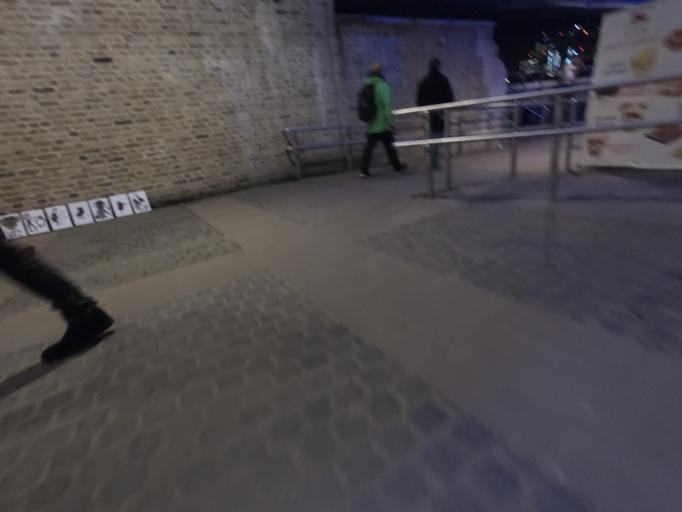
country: GB
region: England
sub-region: Greater London
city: Islington
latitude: 51.5441
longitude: -0.0922
